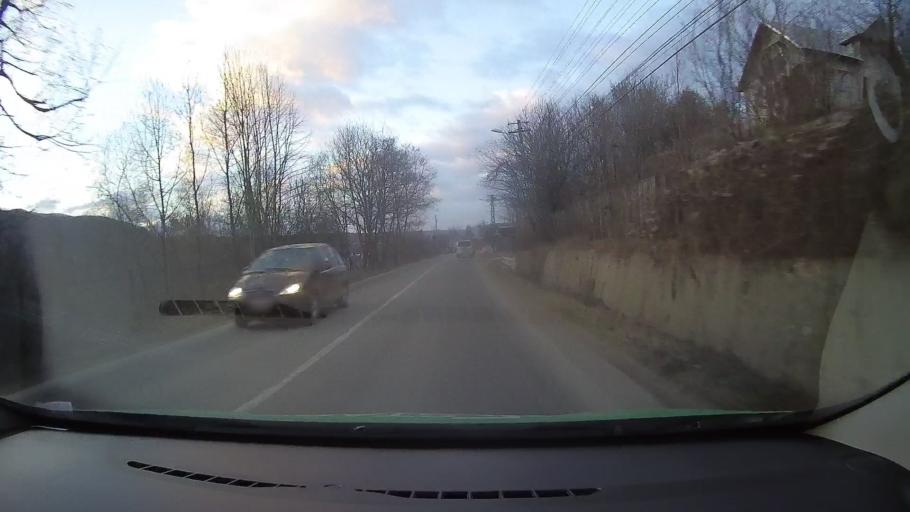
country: RO
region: Dambovita
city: Iedera de Jos
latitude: 45.0189
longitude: 25.6384
